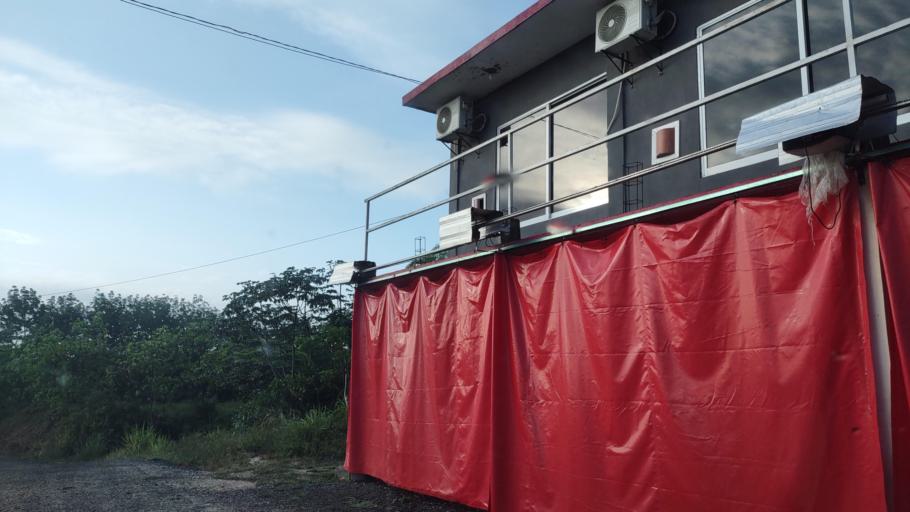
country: MX
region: Veracruz
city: Las Choapas
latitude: 17.8811
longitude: -94.1020
